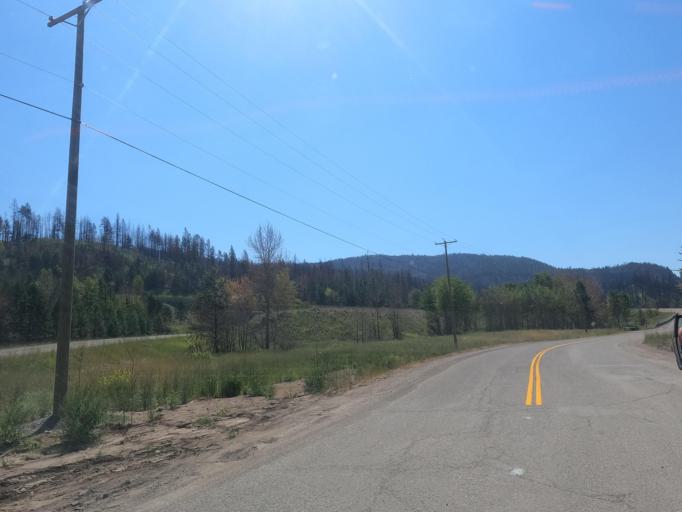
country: CA
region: British Columbia
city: Merritt
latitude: 49.8853
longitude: -120.9030
